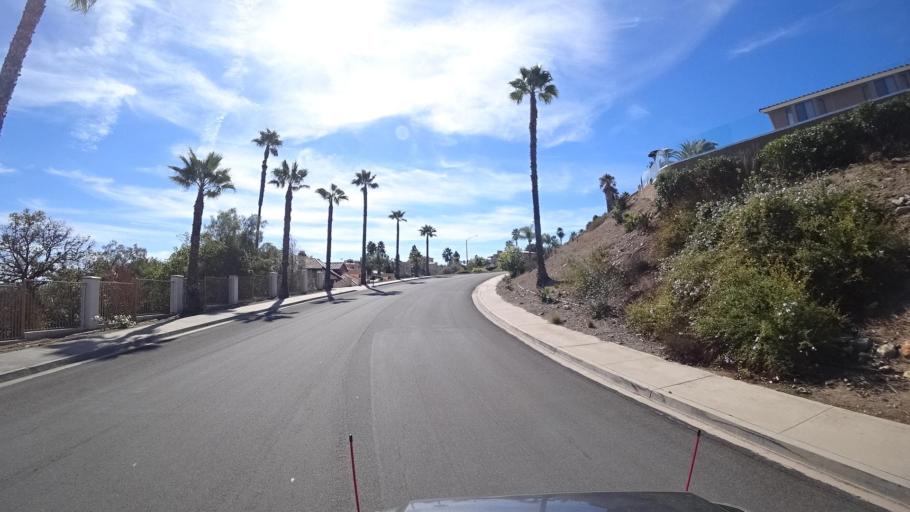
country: US
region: California
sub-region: San Diego County
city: Rancho San Diego
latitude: 32.7570
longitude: -116.9500
